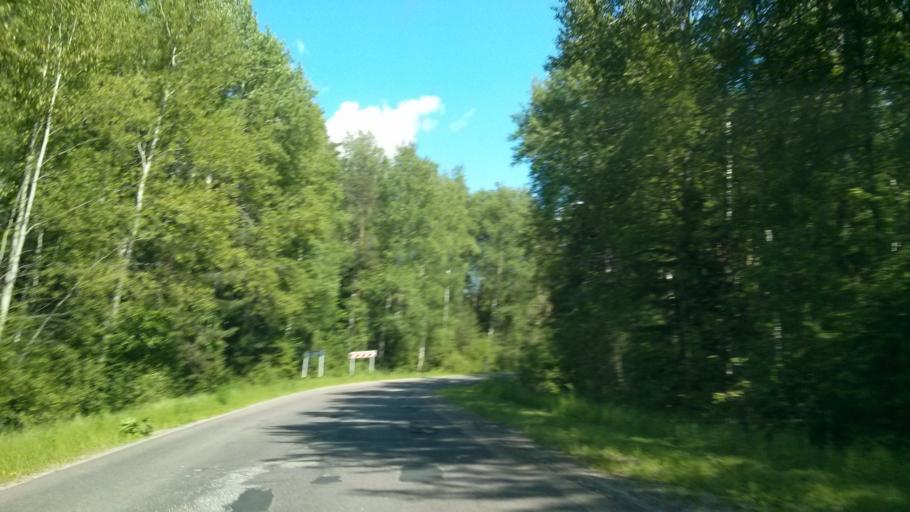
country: RU
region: Vladimir
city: Melenki
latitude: 55.3318
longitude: 41.6947
